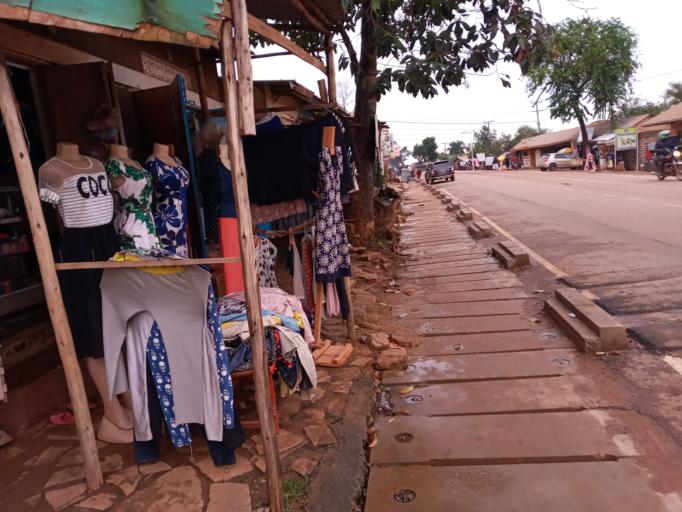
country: UG
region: Central Region
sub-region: Wakiso District
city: Bweyogerere
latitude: 0.3339
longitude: 32.6713
